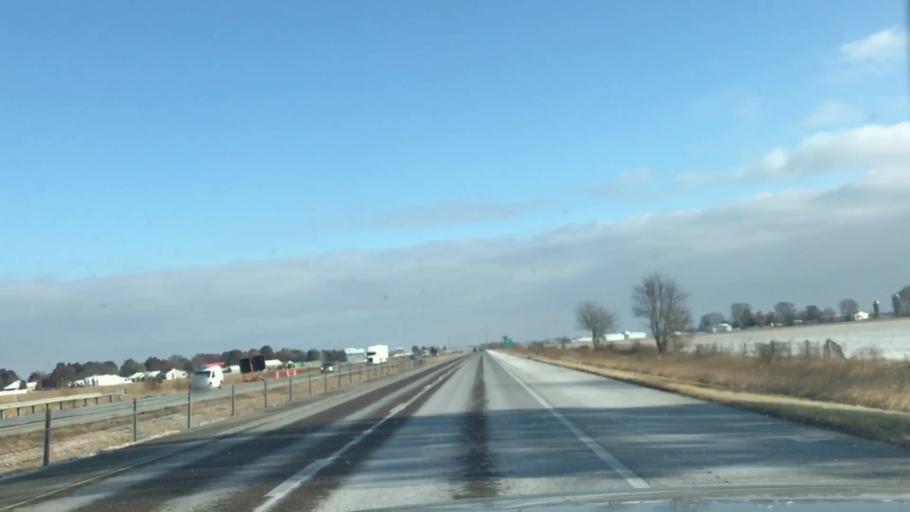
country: US
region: Illinois
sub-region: Madison County
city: Worden
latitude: 38.8768
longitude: -89.8465
